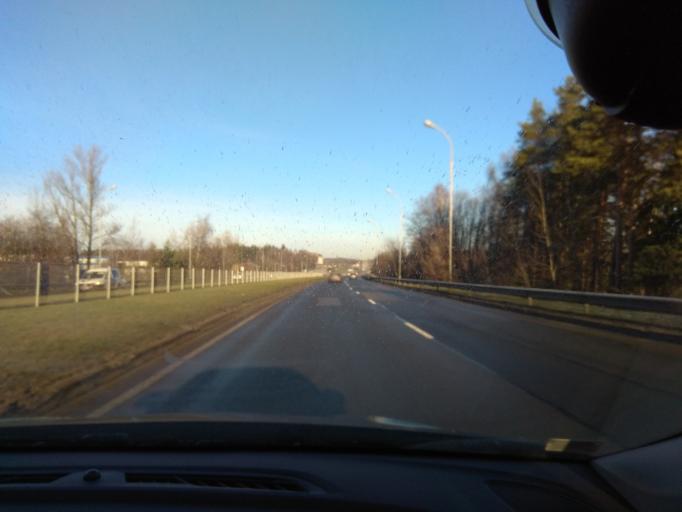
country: LT
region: Vilnius County
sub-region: Vilnius
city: Fabijoniskes
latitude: 54.7344
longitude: 25.2654
